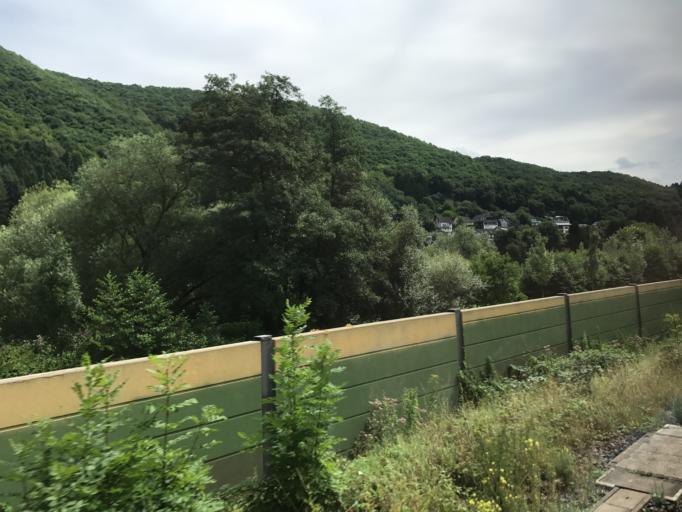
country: DE
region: Rheinland-Pfalz
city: Misselberg
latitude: 50.3244
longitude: 7.7640
